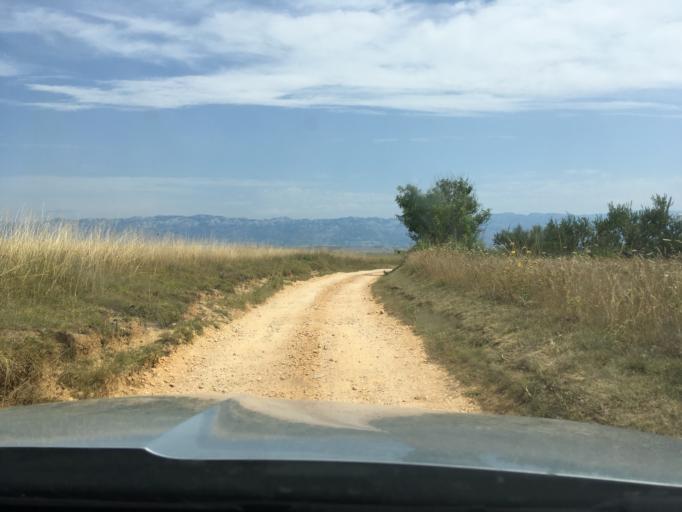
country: HR
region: Zadarska
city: Privlaka
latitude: 44.2644
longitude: 15.1478
